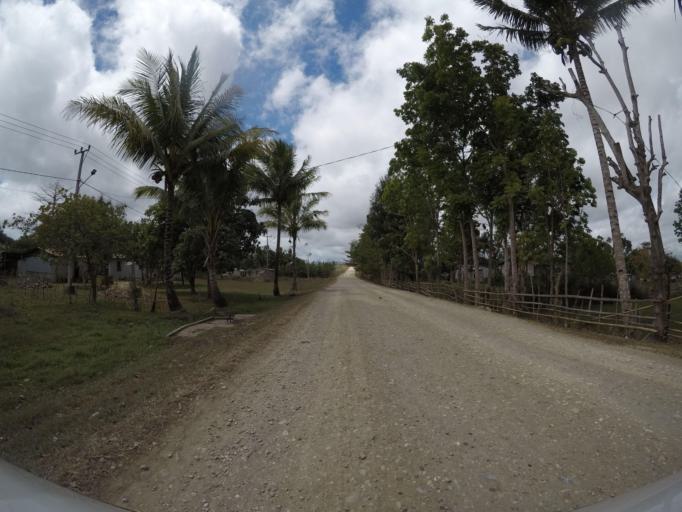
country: TL
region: Lautem
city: Lospalos
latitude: -8.4399
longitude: 126.9839
